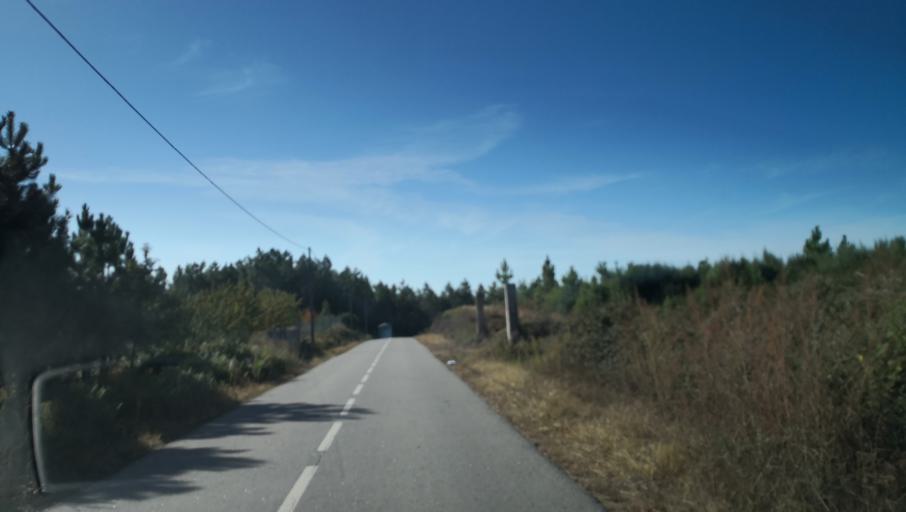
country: PT
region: Vila Real
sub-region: Sabrosa
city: Vilela
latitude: 41.2569
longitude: -7.6227
